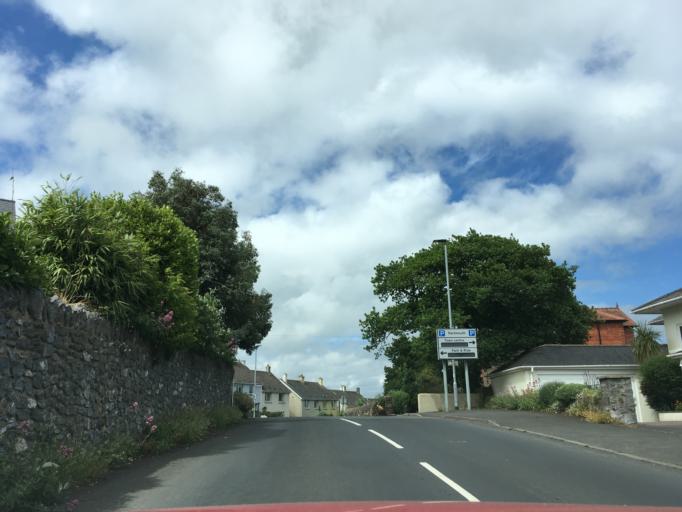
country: GB
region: England
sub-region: Devon
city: Dartmouth
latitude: 50.3497
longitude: -3.5947
